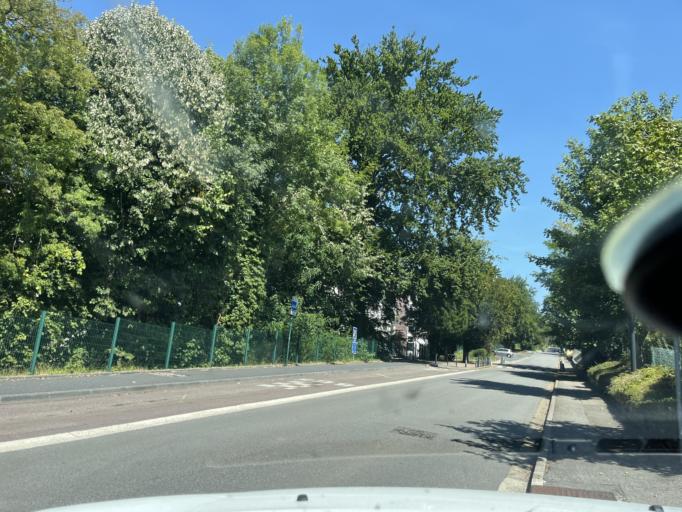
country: FR
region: Haute-Normandie
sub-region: Departement de la Seine-Maritime
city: Lillebonne
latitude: 49.5198
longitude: 0.5409
